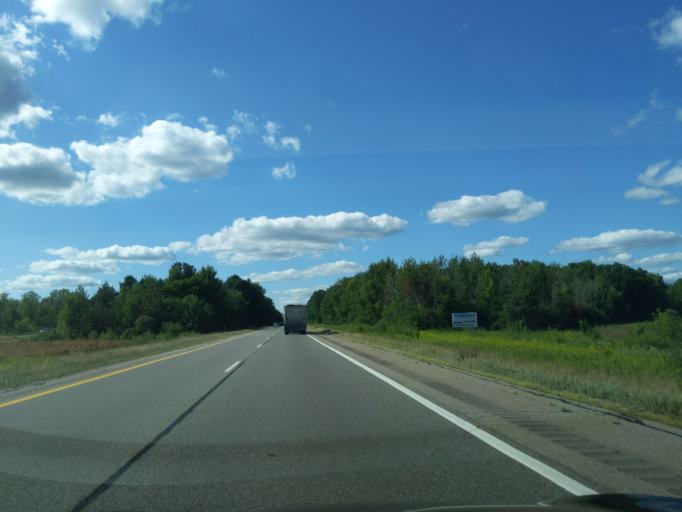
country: US
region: Michigan
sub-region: Muskegon County
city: Fruitport
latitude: 43.1051
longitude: -86.1145
